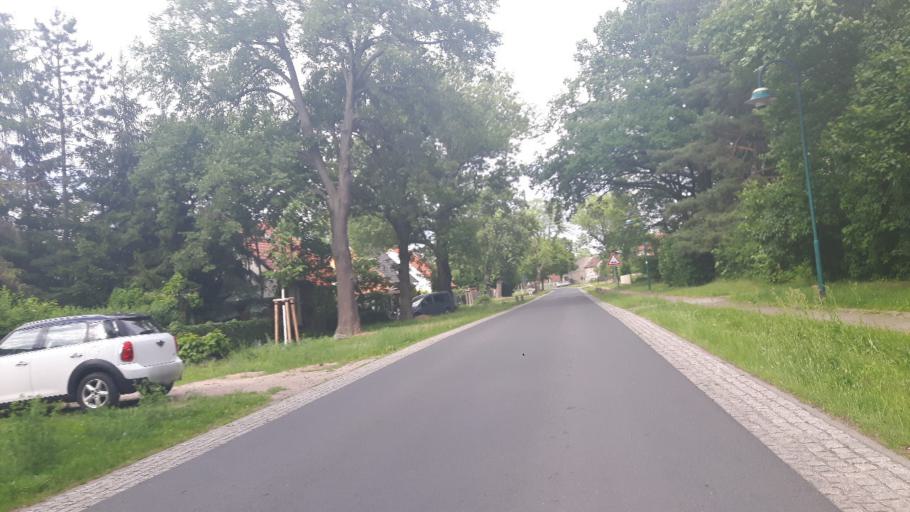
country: DE
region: Brandenburg
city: Bernau bei Berlin
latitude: 52.6635
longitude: 13.6393
